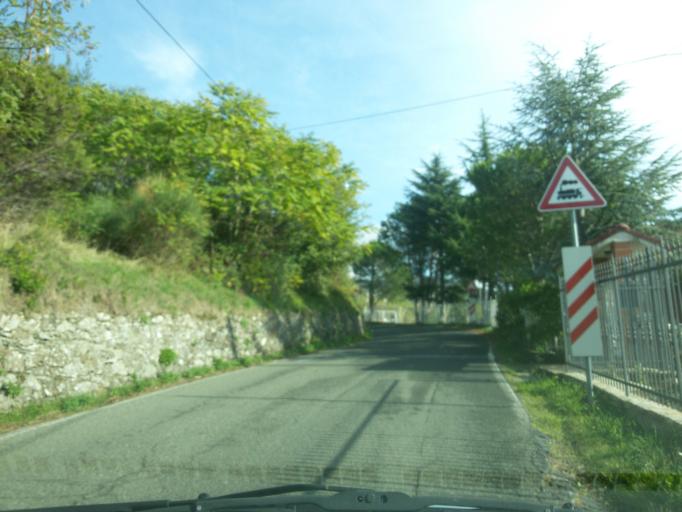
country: IT
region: Liguria
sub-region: Provincia di Genova
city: Piccarello
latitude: 44.4922
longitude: 8.9738
